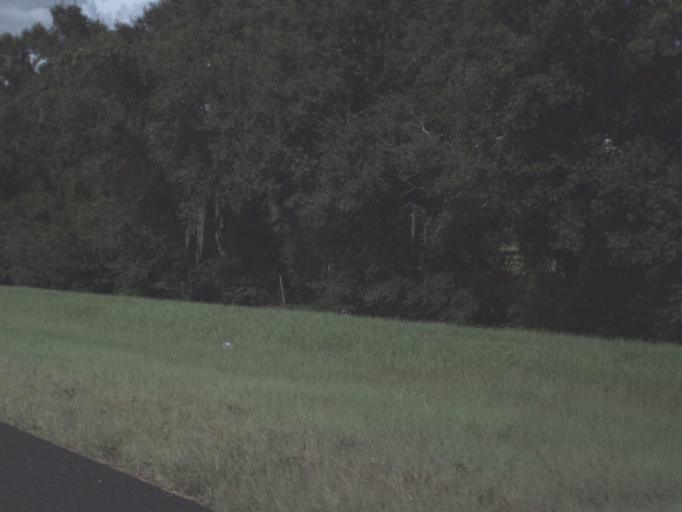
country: US
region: Florida
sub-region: Hardee County
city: Zolfo Springs
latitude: 27.4509
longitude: -81.7967
